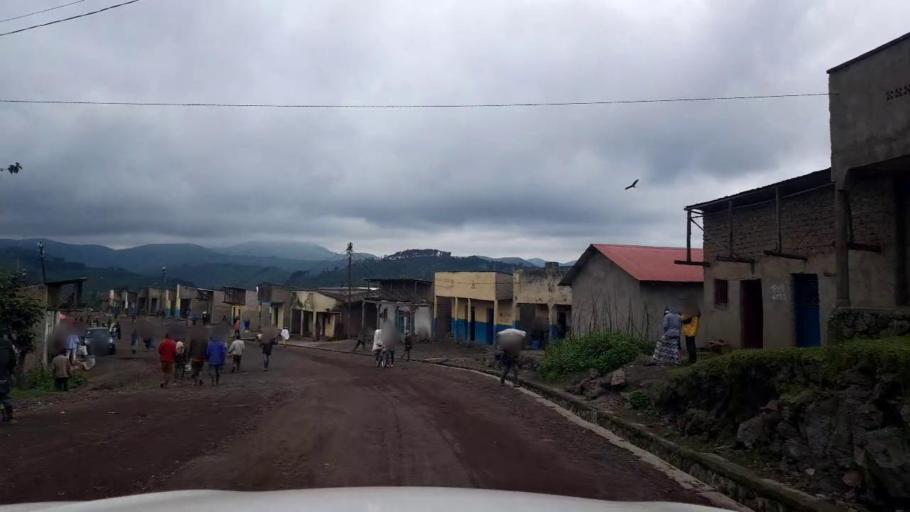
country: RW
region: Northern Province
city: Musanze
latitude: -1.6027
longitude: 29.4513
